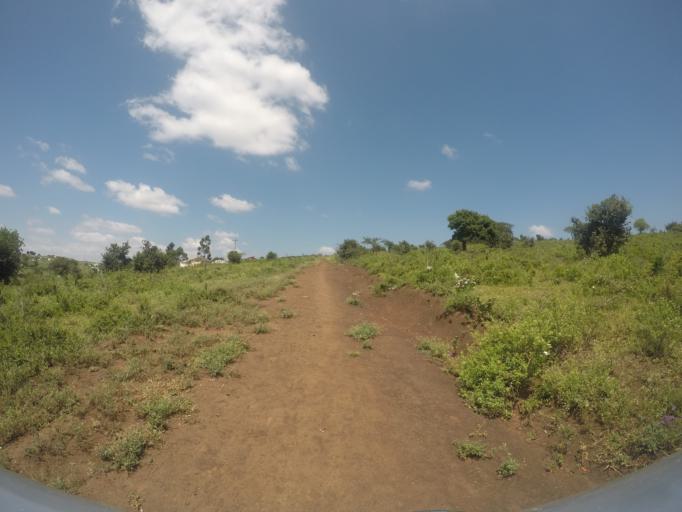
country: ZA
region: KwaZulu-Natal
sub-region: uThungulu District Municipality
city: Empangeni
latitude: -28.6019
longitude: 31.7364
